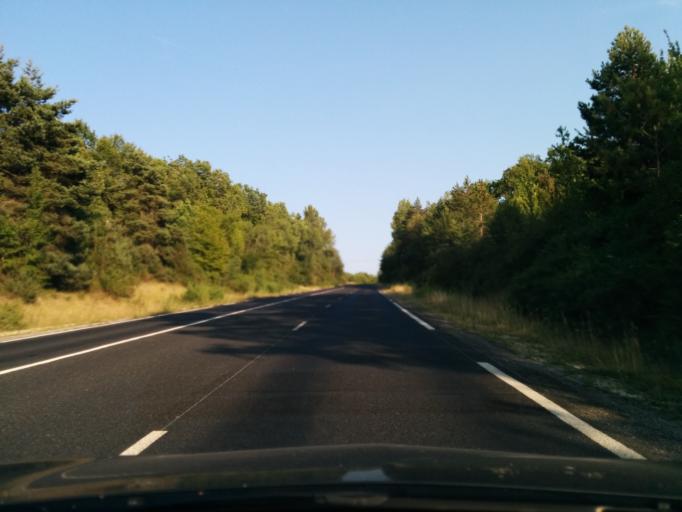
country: FR
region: Midi-Pyrenees
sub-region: Departement du Lot
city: Le Vigan
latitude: 44.7678
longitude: 1.4786
